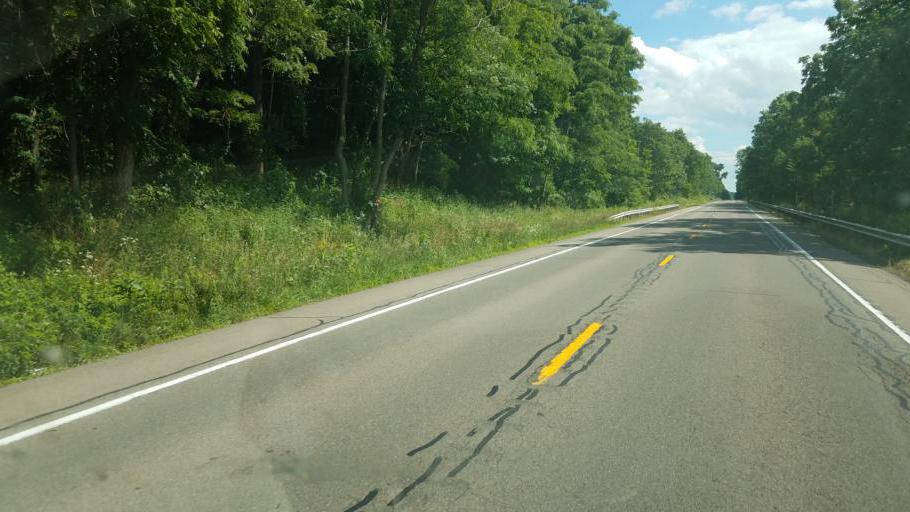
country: US
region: New York
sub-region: Yates County
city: Keuka Park
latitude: 42.5410
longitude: -77.0989
